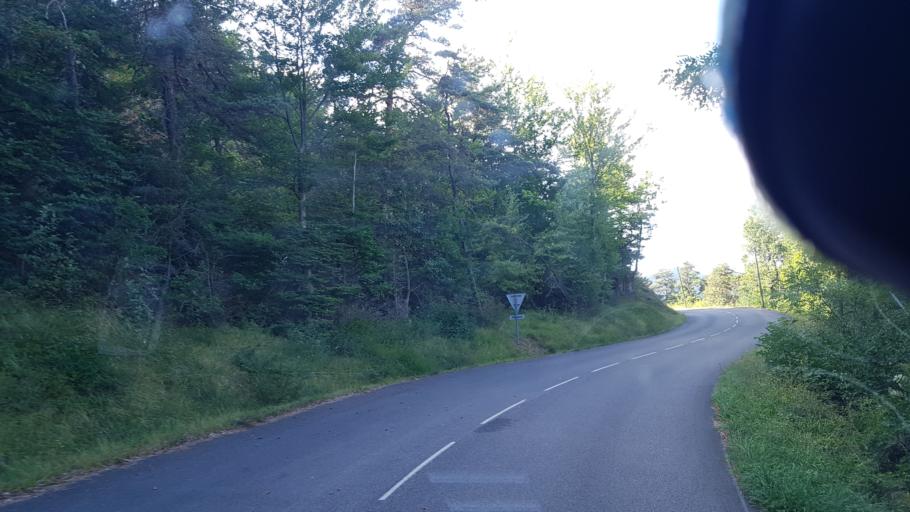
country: FR
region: Rhone-Alpes
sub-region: Departement de l'Isere
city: Mens
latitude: 44.8587
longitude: 5.6808
